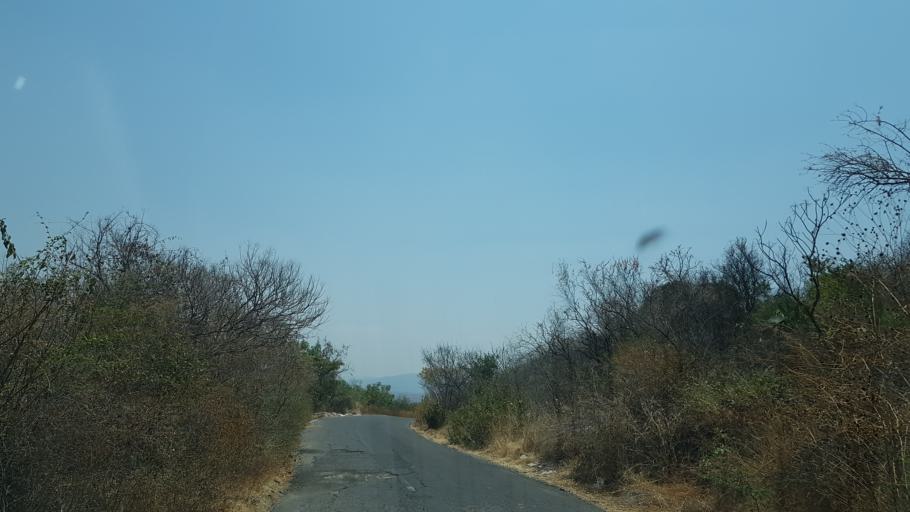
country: MX
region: Puebla
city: Huaquechula
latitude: 18.7937
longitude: -98.5454
